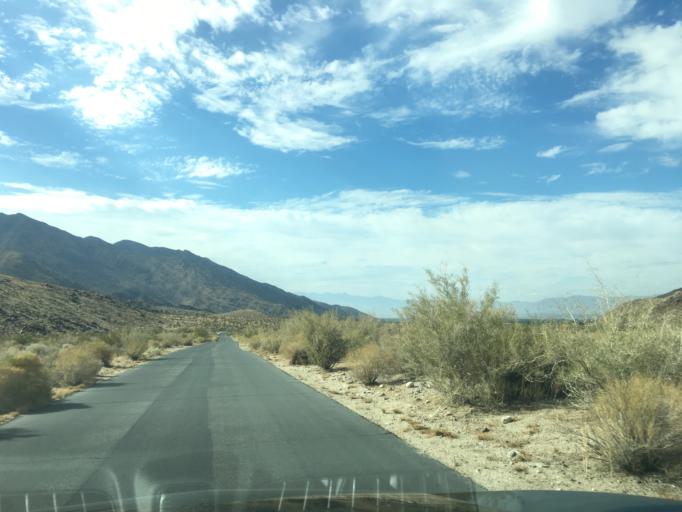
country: US
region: California
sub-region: Riverside County
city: Cathedral City
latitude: 33.7461
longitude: -116.5374
